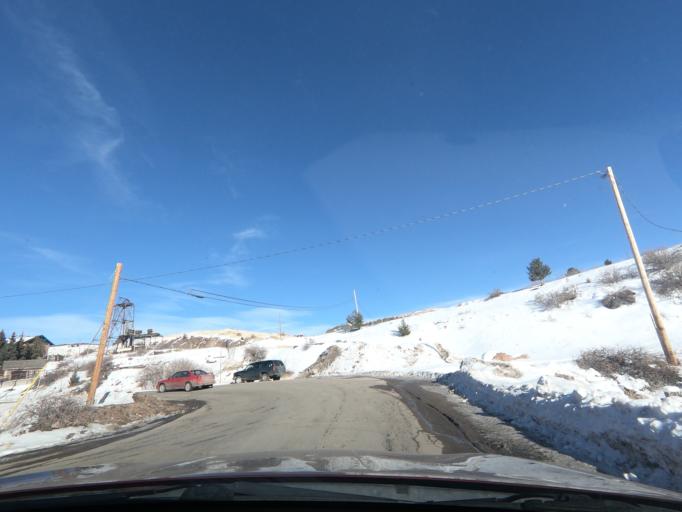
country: US
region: Colorado
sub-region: Teller County
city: Cripple Creek
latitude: 38.7459
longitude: -105.1731
